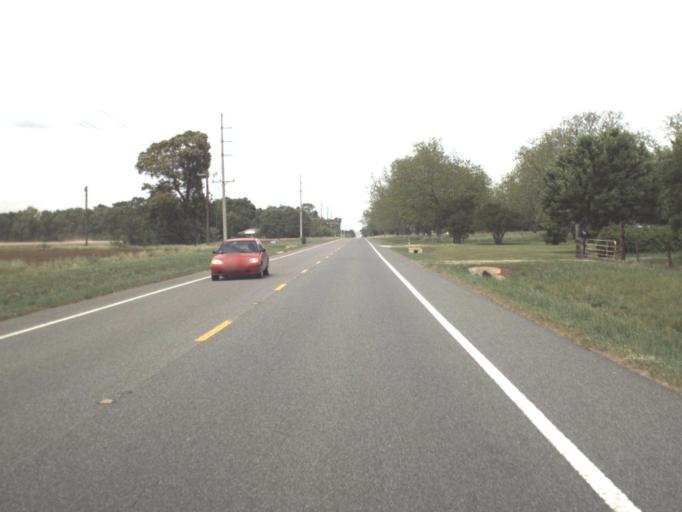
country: US
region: Florida
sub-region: Santa Rosa County
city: Point Baker
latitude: 30.7906
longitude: -87.0923
